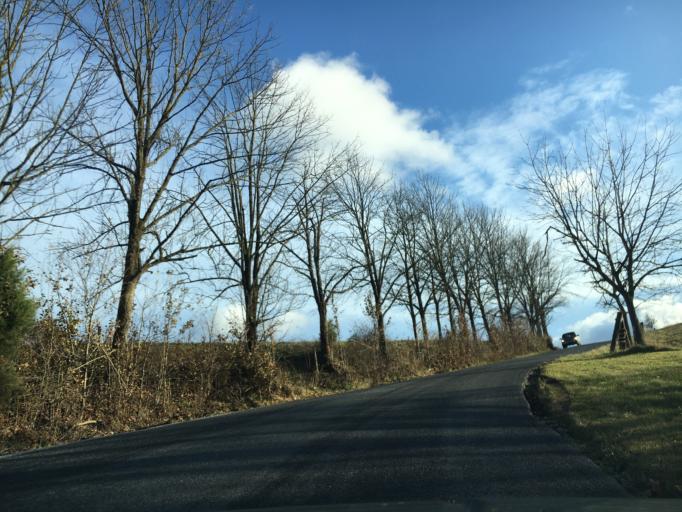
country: US
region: Pennsylvania
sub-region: Carbon County
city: Lehighton
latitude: 40.8043
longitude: -75.7327
